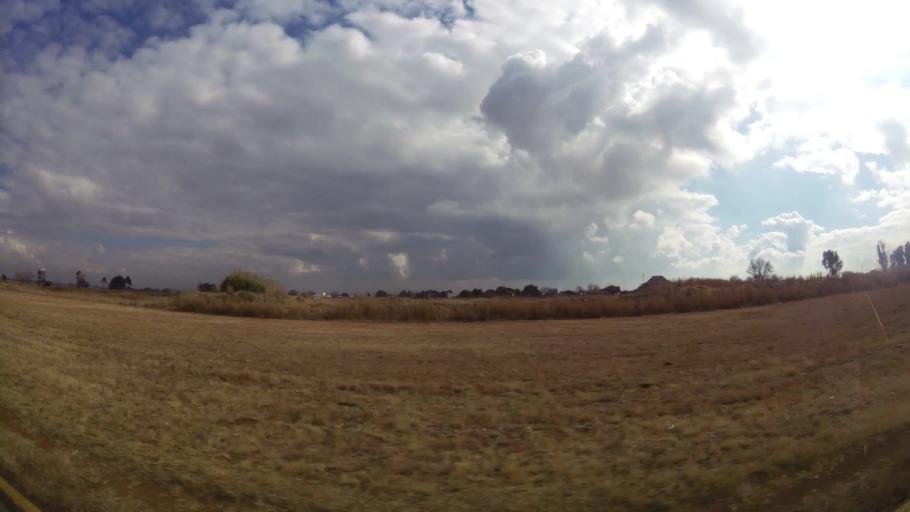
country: ZA
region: Gauteng
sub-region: Sedibeng District Municipality
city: Meyerton
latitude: -26.6171
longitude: 28.0602
